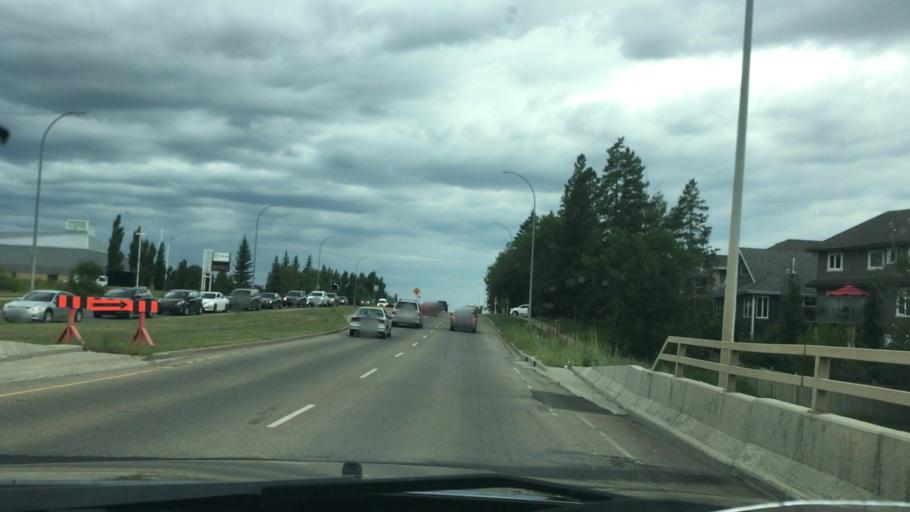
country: CA
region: Alberta
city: Beaumont
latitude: 53.4250
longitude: -113.4993
